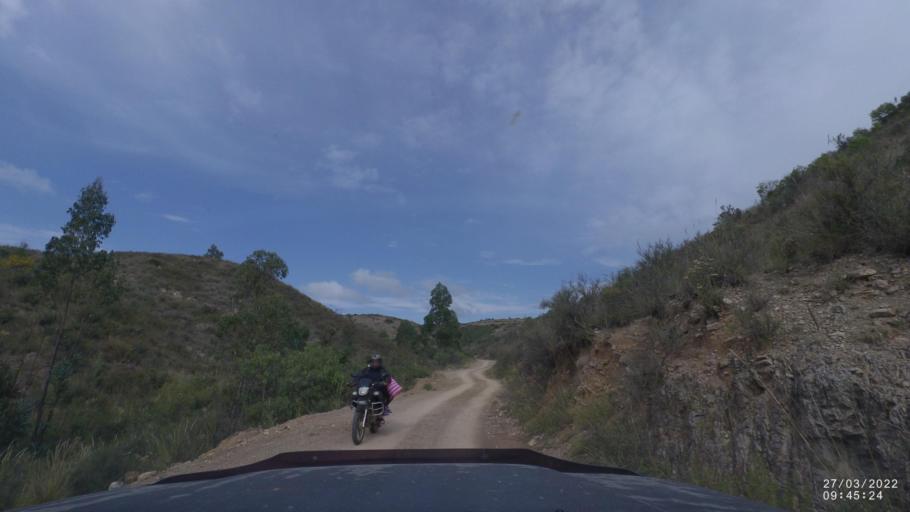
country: BO
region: Cochabamba
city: Cliza
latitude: -17.7509
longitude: -65.9132
